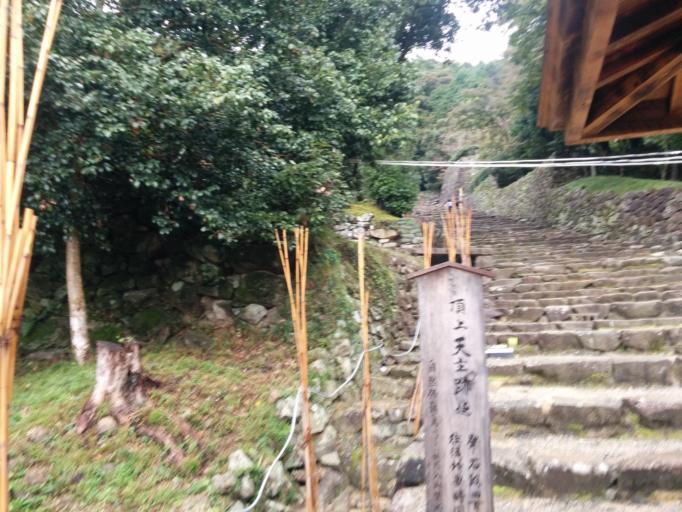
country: JP
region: Shiga Prefecture
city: Omihachiman
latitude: 35.1536
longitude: 136.1391
